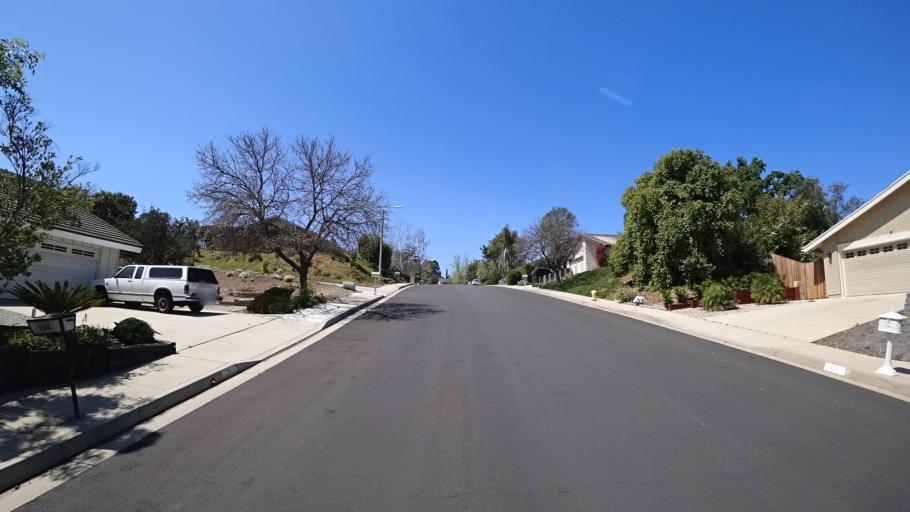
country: US
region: California
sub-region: Ventura County
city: Casa Conejo
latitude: 34.2027
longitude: -118.8924
